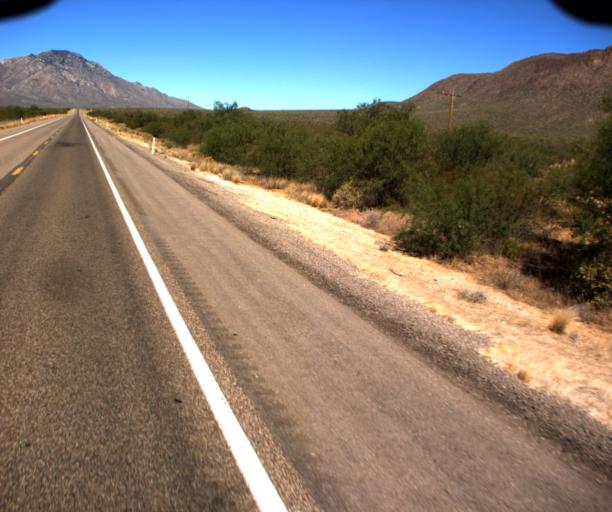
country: US
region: Arizona
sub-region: Pima County
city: Three Points
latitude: 32.0504
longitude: -111.4205
